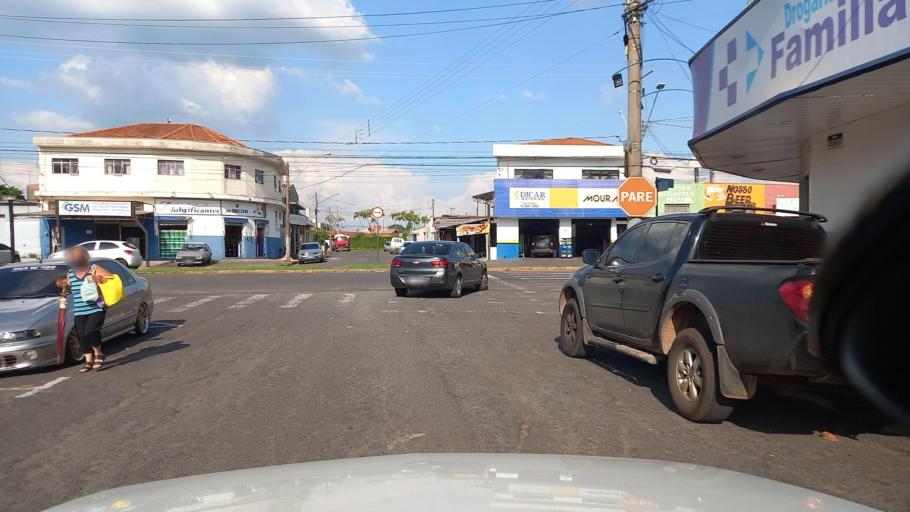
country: BR
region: Sao Paulo
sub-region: Moji-Guacu
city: Mogi-Gaucu
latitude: -22.3508
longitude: -46.9465
